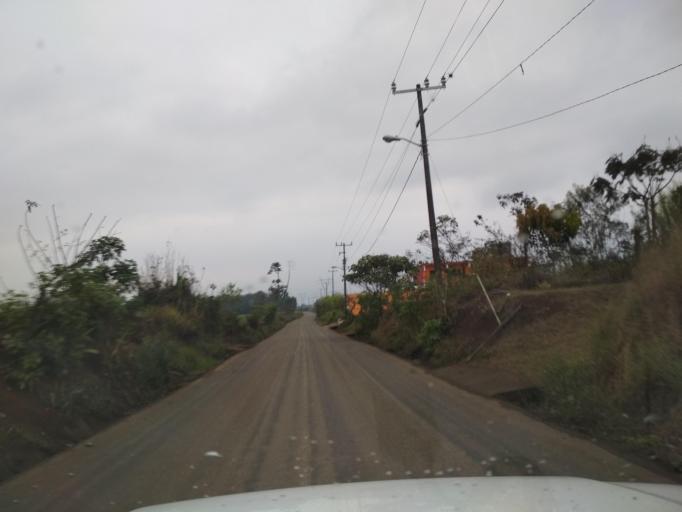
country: MX
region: Veracruz
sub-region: Cordoba
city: Veinte de Noviembre
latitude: 18.8718
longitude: -96.9657
